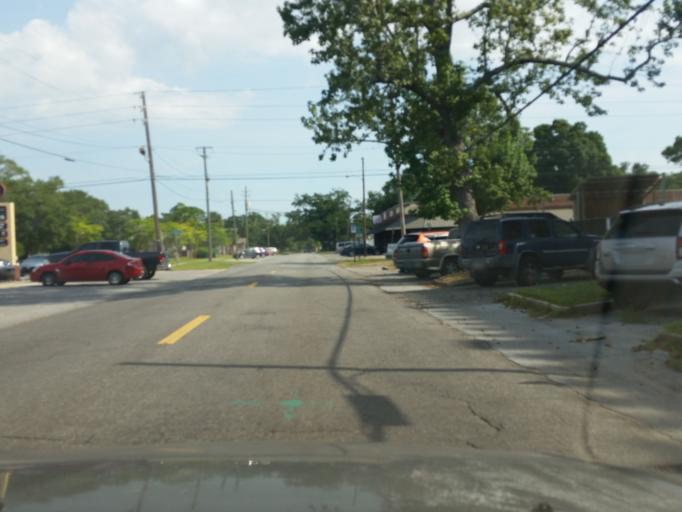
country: US
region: Florida
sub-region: Escambia County
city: Pensacola
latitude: 30.4262
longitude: -87.2031
